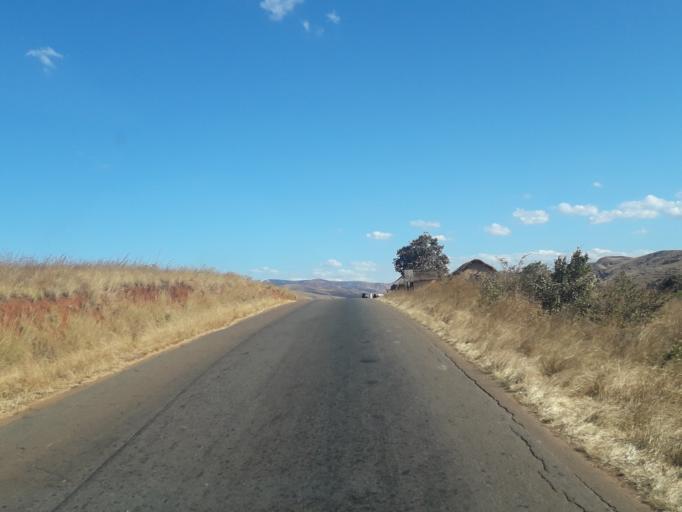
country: MG
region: Analamanga
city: Ankazobe
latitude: -17.6662
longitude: 46.9847
